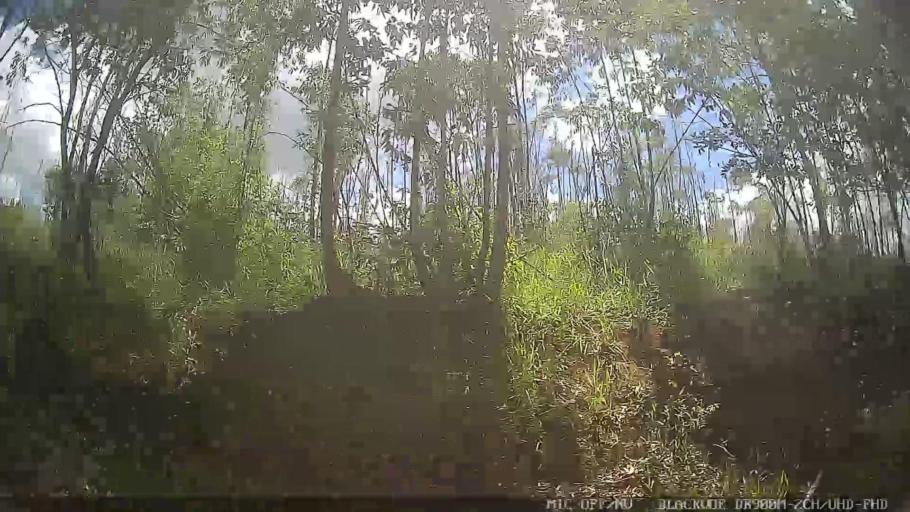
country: BR
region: Sao Paulo
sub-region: Braganca Paulista
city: Braganca Paulista
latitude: -22.9955
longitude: -46.4557
